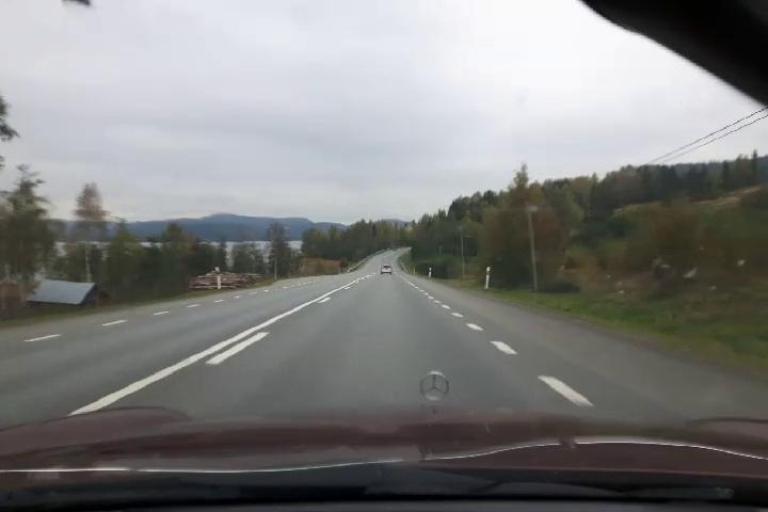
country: SE
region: Vaesternorrland
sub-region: Kramfors Kommun
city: Nordingra
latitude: 63.0156
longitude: 18.2925
